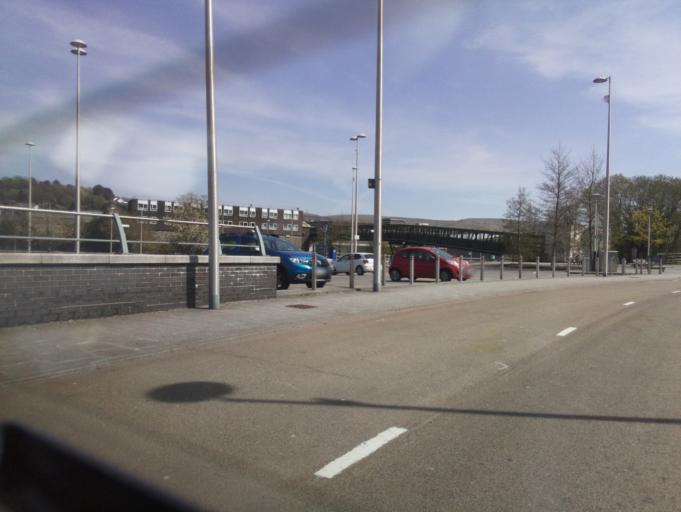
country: GB
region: Wales
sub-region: Merthyr Tydfil County Borough
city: Merthyr Tydfil
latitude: 51.7453
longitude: -3.3824
